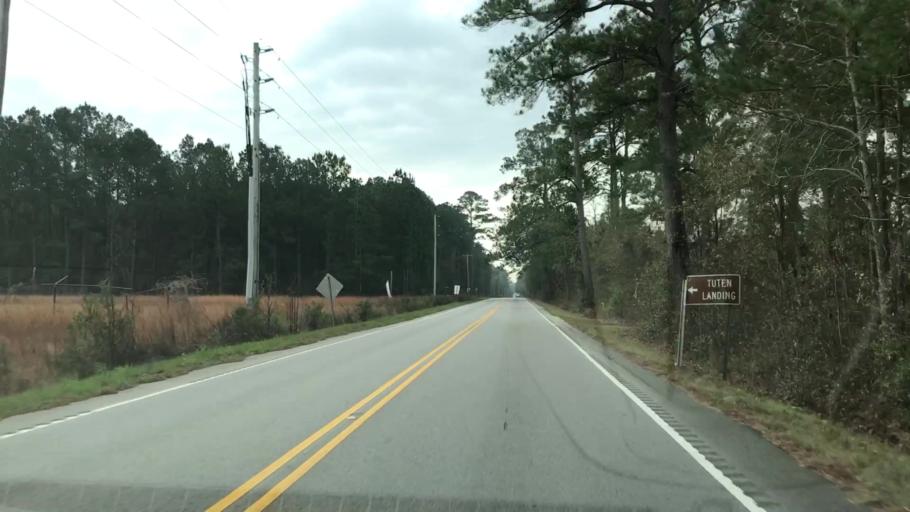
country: US
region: South Carolina
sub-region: Jasper County
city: Ridgeland
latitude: 32.5161
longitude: -80.8897
